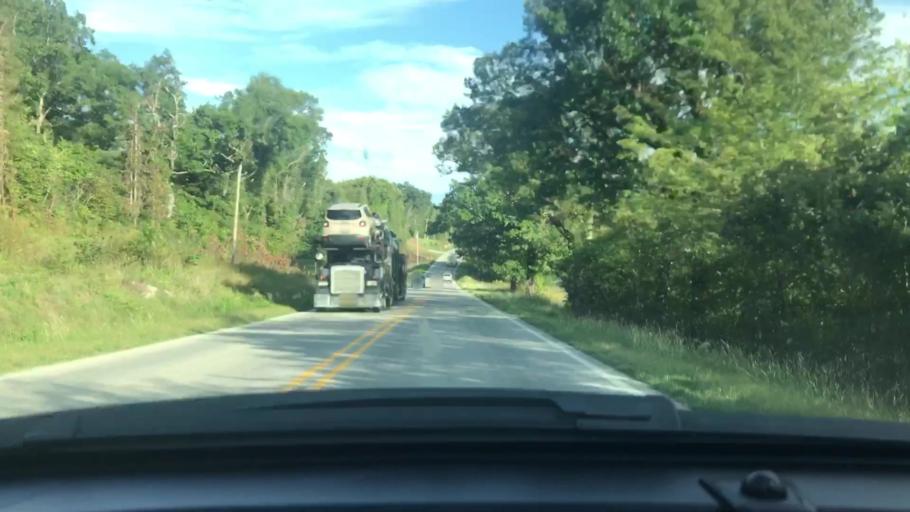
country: US
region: Arkansas
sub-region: Sharp County
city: Cherokee Village
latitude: 36.3085
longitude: -91.4576
